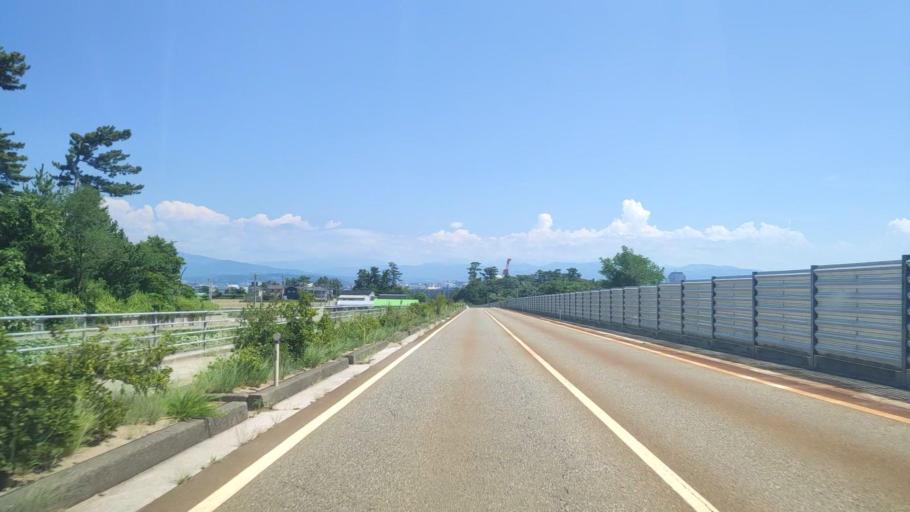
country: JP
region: Ishikawa
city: Kanazawa-shi
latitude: 36.6215
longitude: 136.6179
